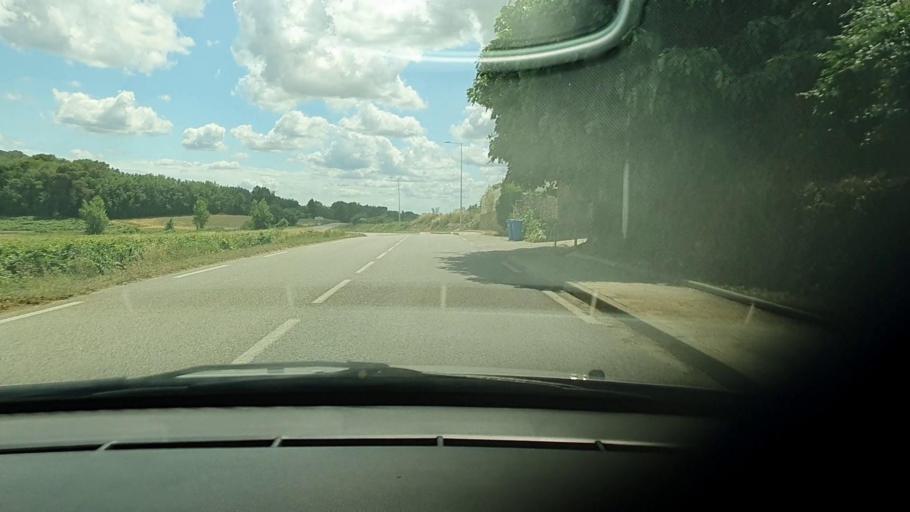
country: FR
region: Languedoc-Roussillon
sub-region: Departement du Gard
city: Moussac
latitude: 44.0260
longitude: 4.2338
